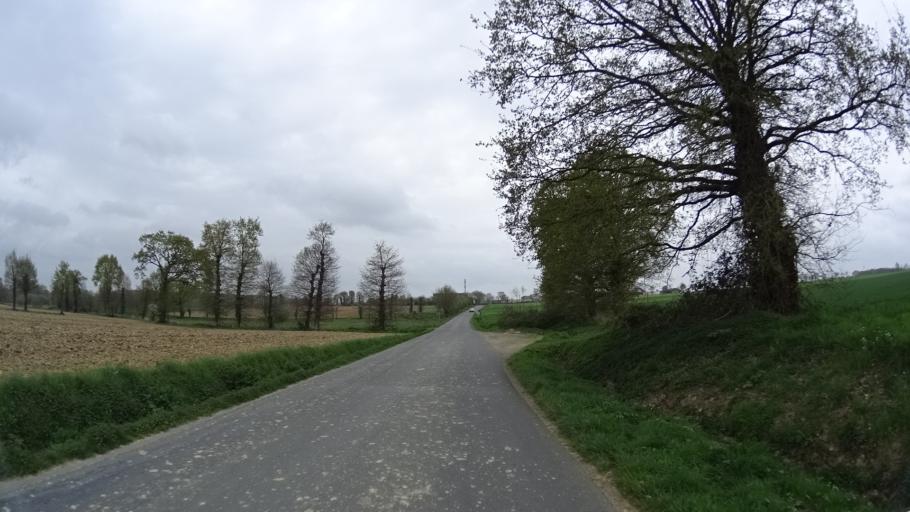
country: FR
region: Brittany
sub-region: Departement d'Ille-et-Vilaine
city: La Chapelle-Thouarault
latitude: 48.1156
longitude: -1.8712
